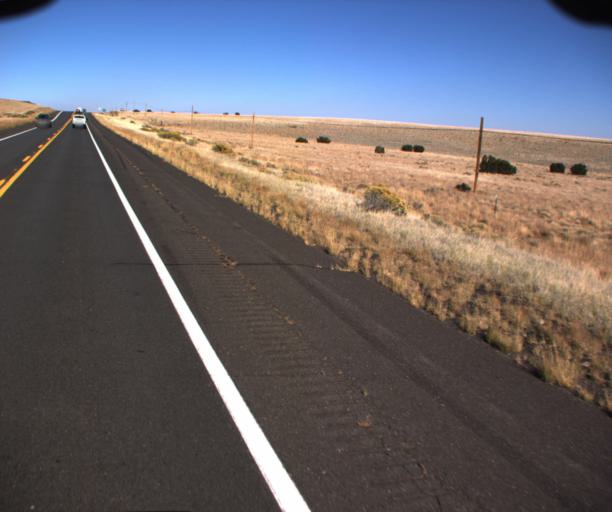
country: US
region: Arizona
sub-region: Coconino County
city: Flagstaff
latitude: 35.5638
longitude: -111.5335
